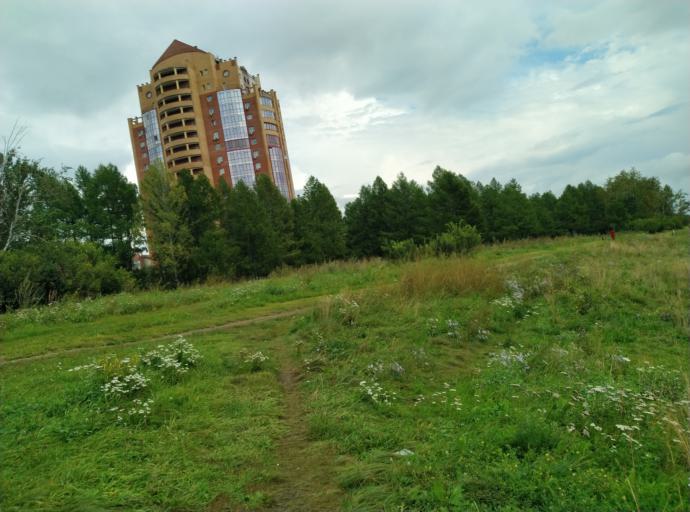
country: RU
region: Krasnoyarskiy
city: Krasnoyarsk
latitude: 55.9833
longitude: 92.7476
